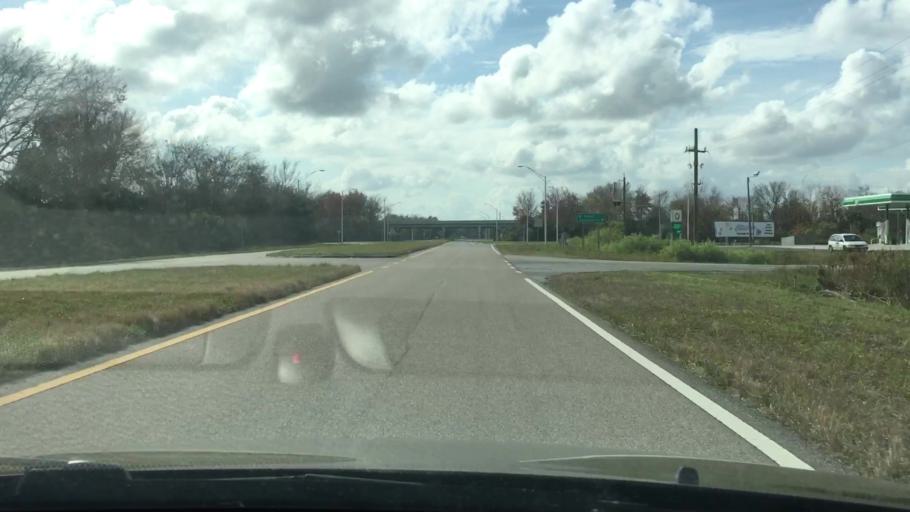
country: US
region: Florida
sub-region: Volusia County
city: Oak Hill
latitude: 28.7733
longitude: -80.8916
